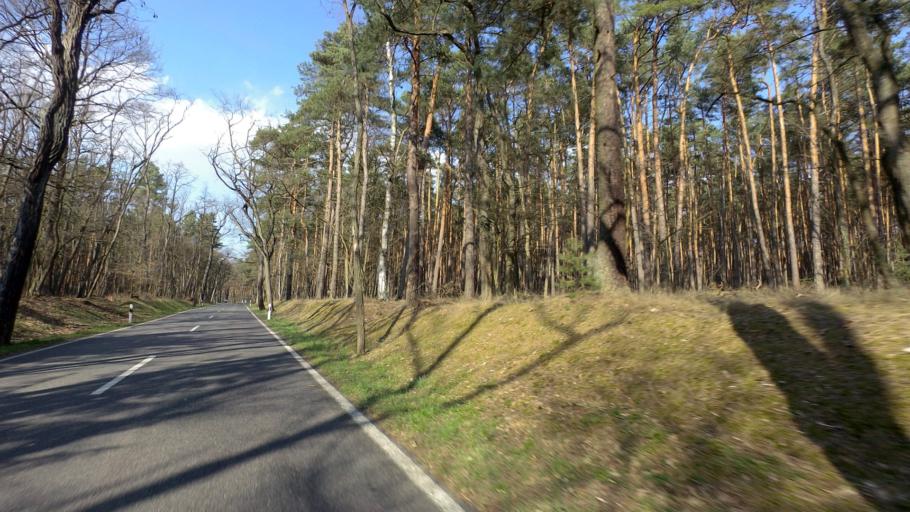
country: DE
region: Brandenburg
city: Dahme
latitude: 51.9164
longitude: 13.4829
